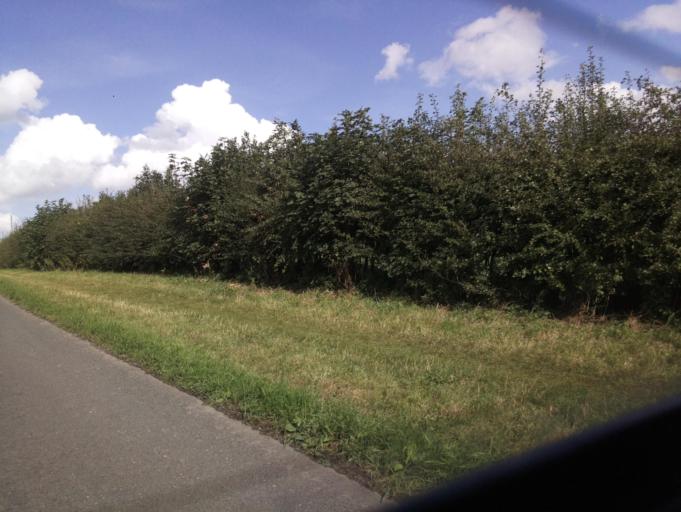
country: GB
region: England
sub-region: North Yorkshire
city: Leyburn
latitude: 54.3174
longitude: -1.8232
